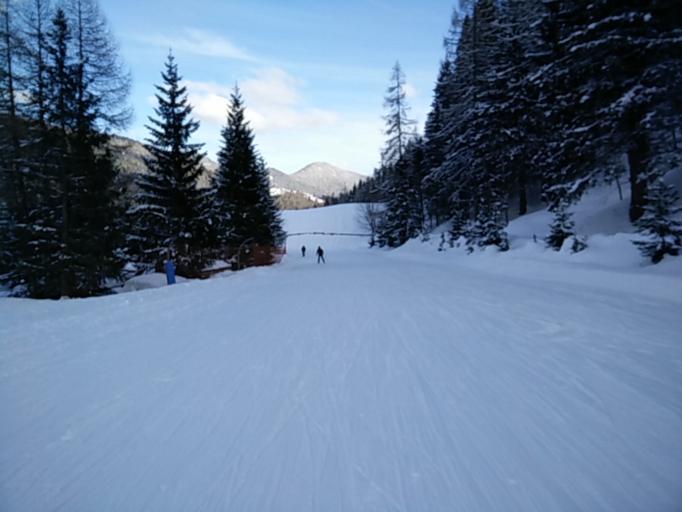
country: IT
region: Veneto
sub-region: Provincia di Belluno
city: Fusine
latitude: 46.3913
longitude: 12.0979
